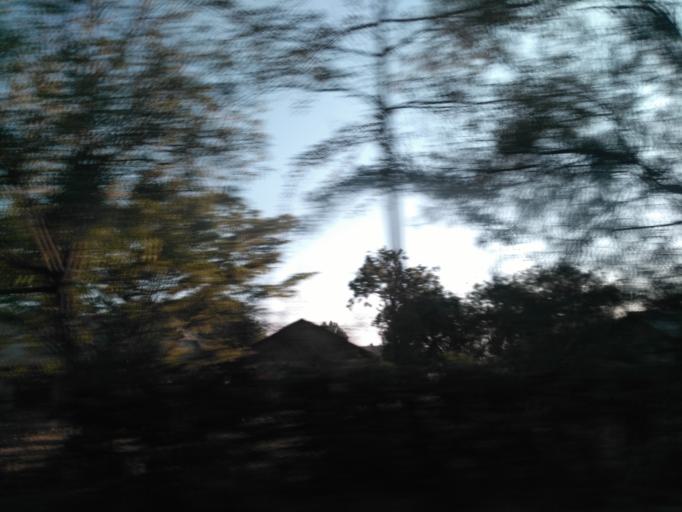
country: TZ
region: Dodoma
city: Dodoma
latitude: -6.1721
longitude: 35.7371
